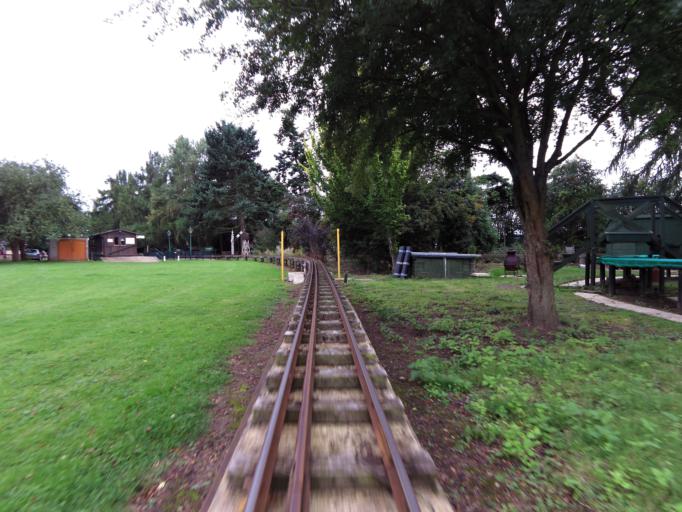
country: GB
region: England
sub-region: Hertfordshire
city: Shenley AV
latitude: 51.7370
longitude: -0.2670
